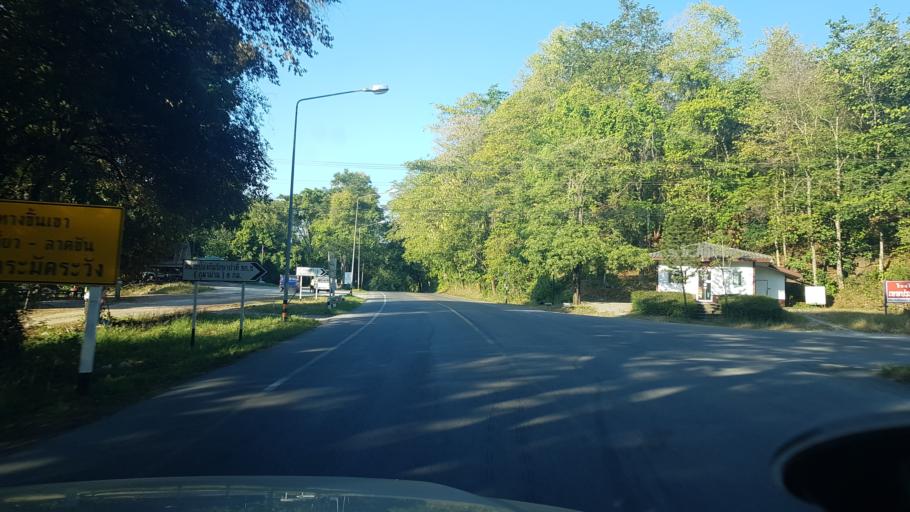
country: TH
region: Khon Kaen
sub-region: Amphoe Phu Pha Man
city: Phu Pha Man
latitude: 16.6511
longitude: 101.8019
